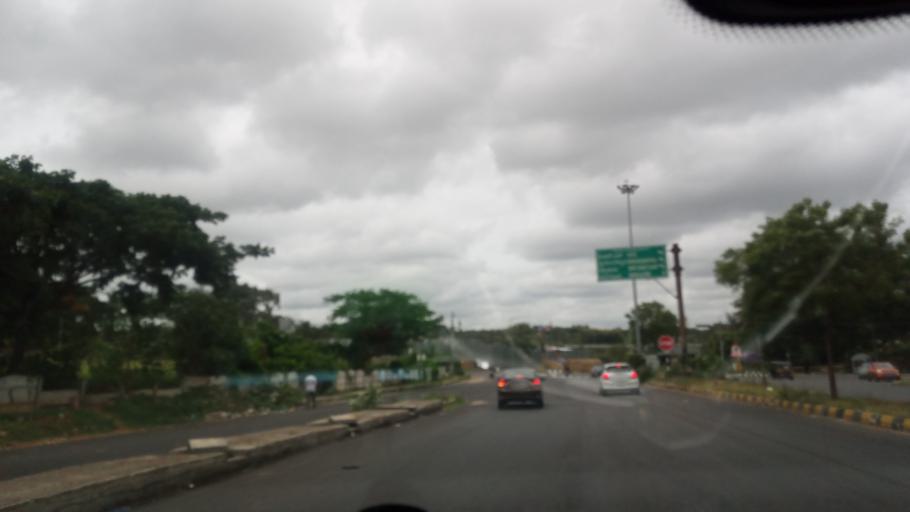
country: IN
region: Karnataka
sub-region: Mysore
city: Mysore
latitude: 12.3518
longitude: 76.6281
